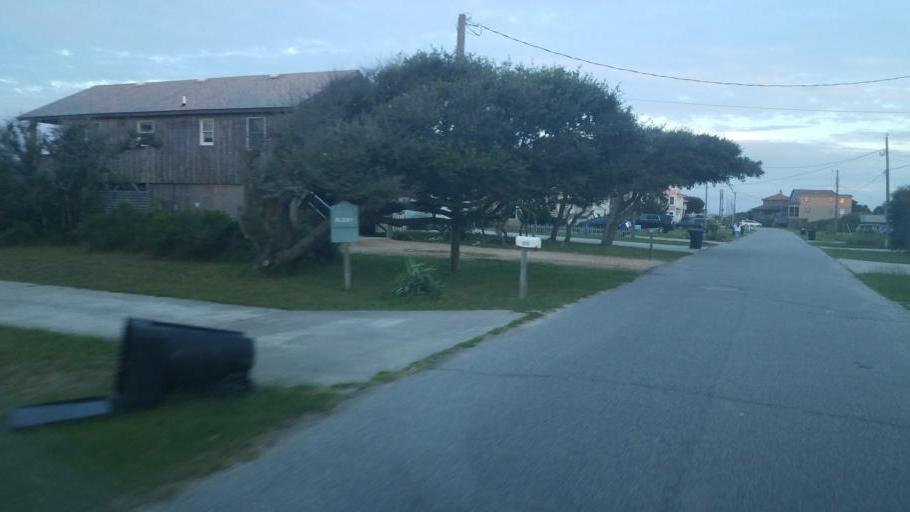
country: US
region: North Carolina
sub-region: Dare County
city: Kitty Hawk
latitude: 36.0772
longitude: -75.6990
